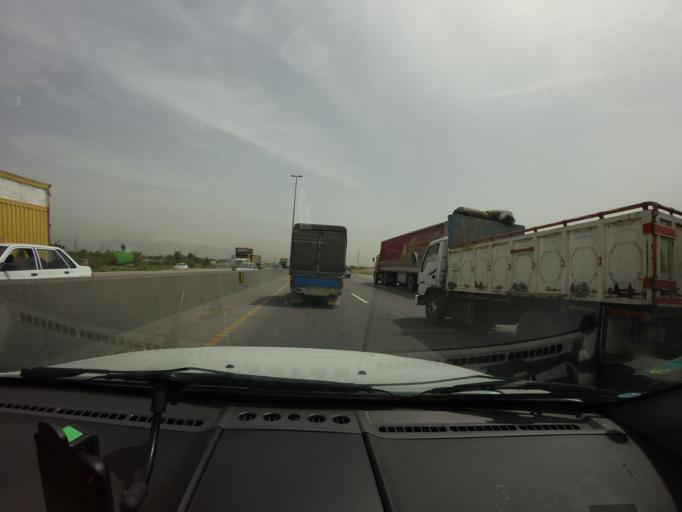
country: IR
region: Tehran
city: Eslamshahr
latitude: 35.6081
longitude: 51.2008
